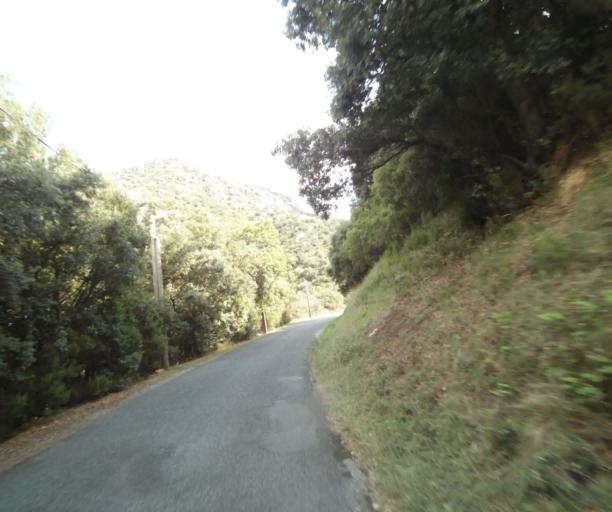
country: FR
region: Languedoc-Roussillon
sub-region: Departement des Pyrenees-Orientales
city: Sorede
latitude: 42.5167
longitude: 2.9876
